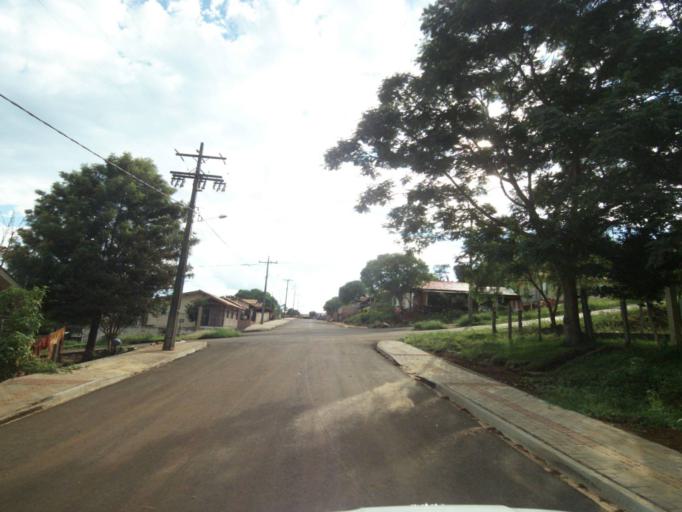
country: BR
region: Parana
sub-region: Laranjeiras Do Sul
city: Laranjeiras do Sul
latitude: -25.4941
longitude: -52.5235
